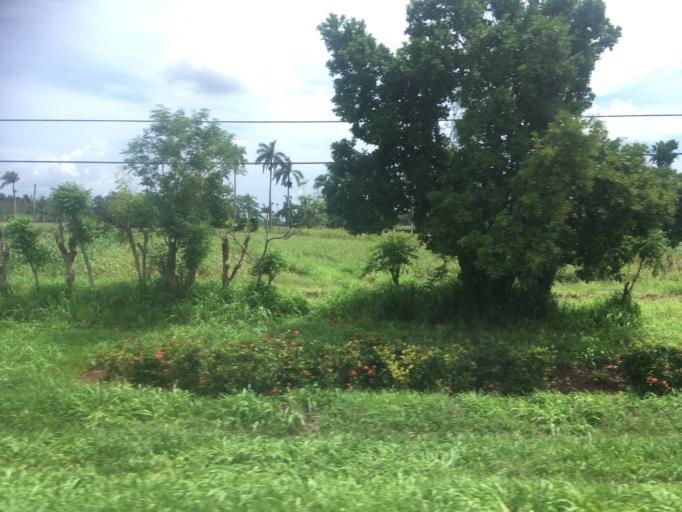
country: CU
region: Matanzas
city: Perico
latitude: 22.7749
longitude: -81.0311
